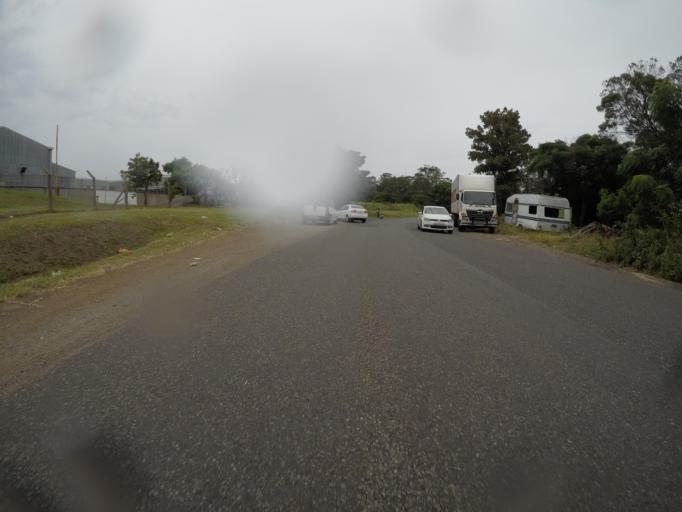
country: ZA
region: Eastern Cape
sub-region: Buffalo City Metropolitan Municipality
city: East London
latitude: -32.9782
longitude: 27.8270
